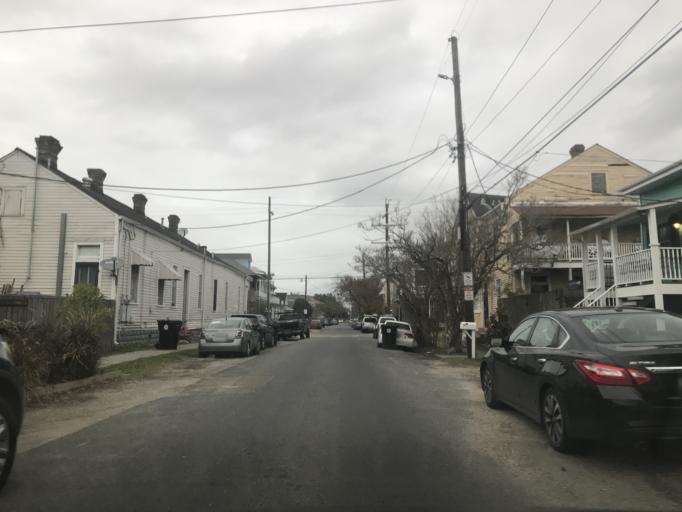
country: US
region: Louisiana
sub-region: Orleans Parish
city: New Orleans
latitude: 29.9655
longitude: -90.0925
